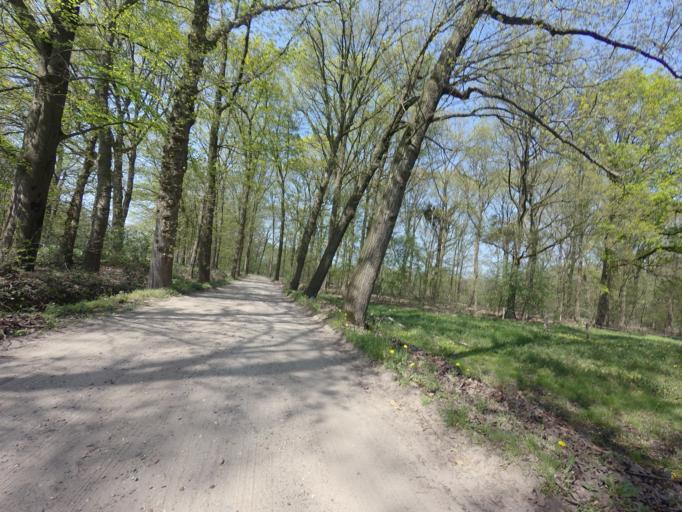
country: NL
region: North Brabant
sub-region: Gemeente Baarle-Nassau
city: Baarle-Nassau
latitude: 51.4854
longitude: 4.9951
